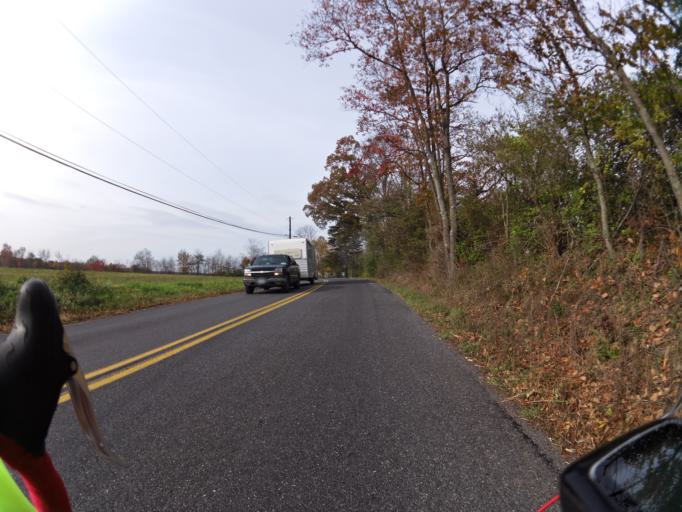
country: US
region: Pennsylvania
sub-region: Union County
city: New Columbia
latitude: 41.0508
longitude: -76.9331
